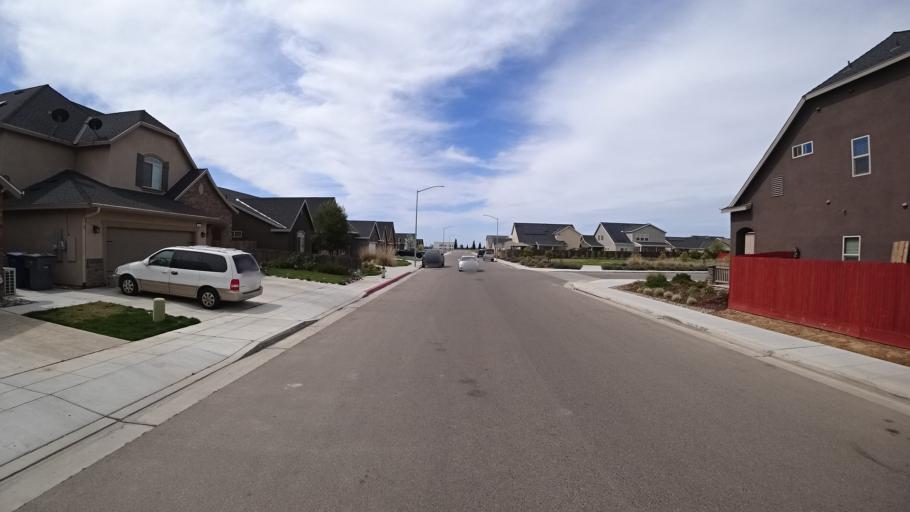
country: US
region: California
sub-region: Fresno County
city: Biola
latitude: 36.8109
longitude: -119.9188
